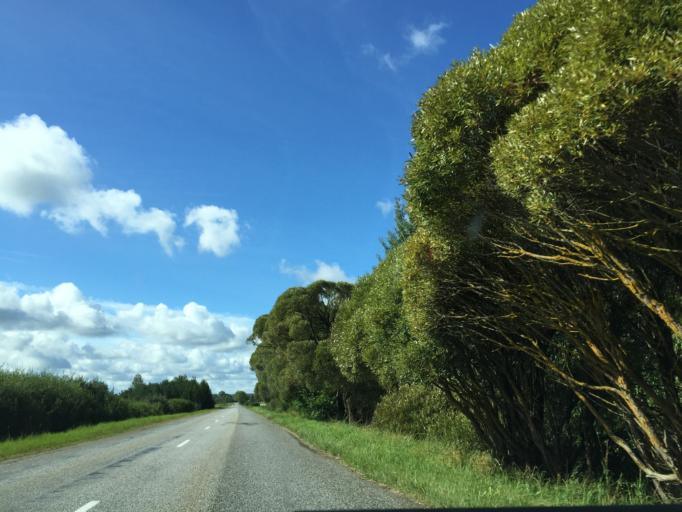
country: LV
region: Kuldigas Rajons
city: Kuldiga
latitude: 56.9779
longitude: 22.0109
